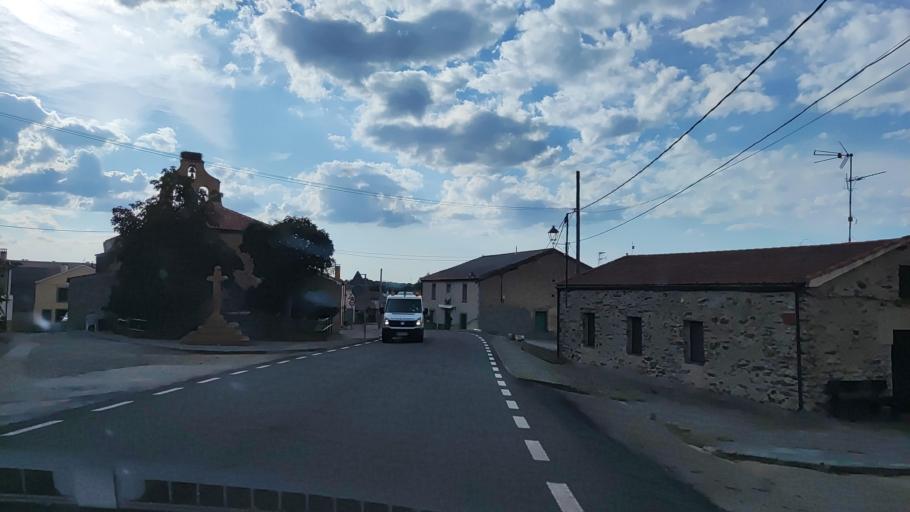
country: ES
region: Castille and Leon
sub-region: Provincia de Salamanca
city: Pastores
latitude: 40.5149
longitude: -6.5091
